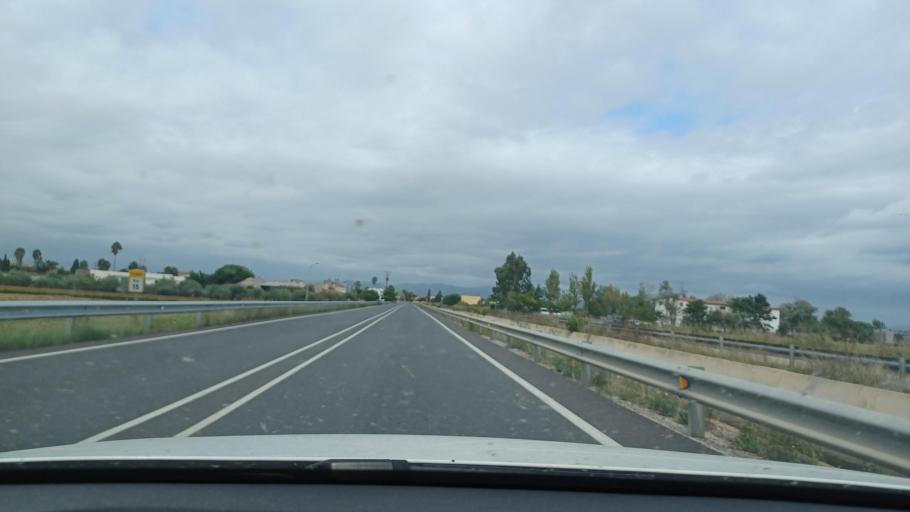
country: ES
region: Catalonia
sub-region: Provincia de Tarragona
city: Deltebre
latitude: 40.7150
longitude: 0.7531
